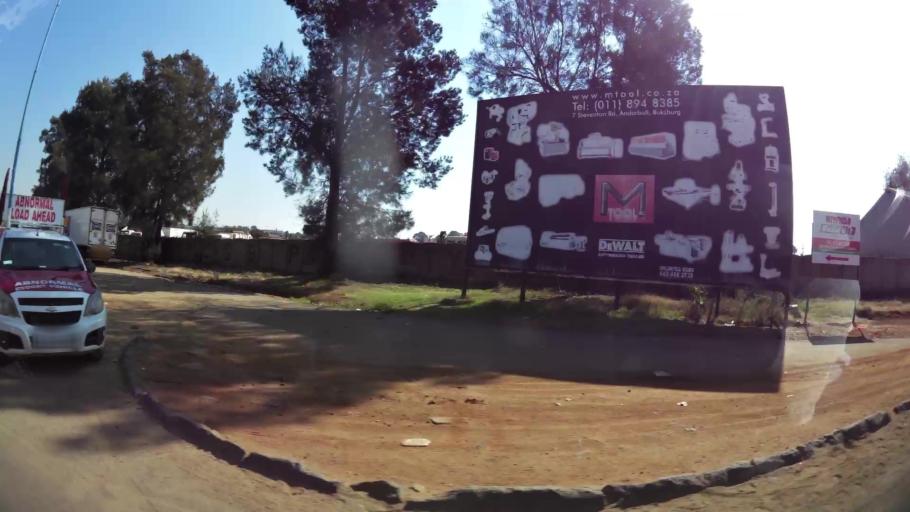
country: ZA
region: Gauteng
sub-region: Ekurhuleni Metropolitan Municipality
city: Boksburg
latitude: -26.1752
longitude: 28.2114
